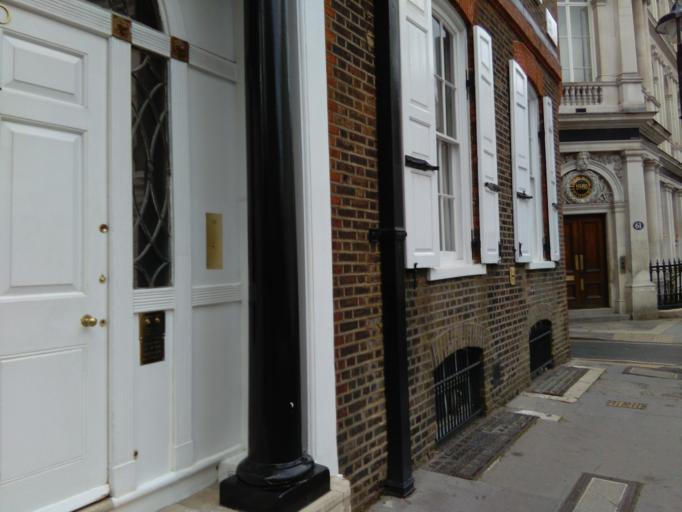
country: GB
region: England
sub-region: Greater London
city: Clerkenwell
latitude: 51.5151
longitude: -0.1125
